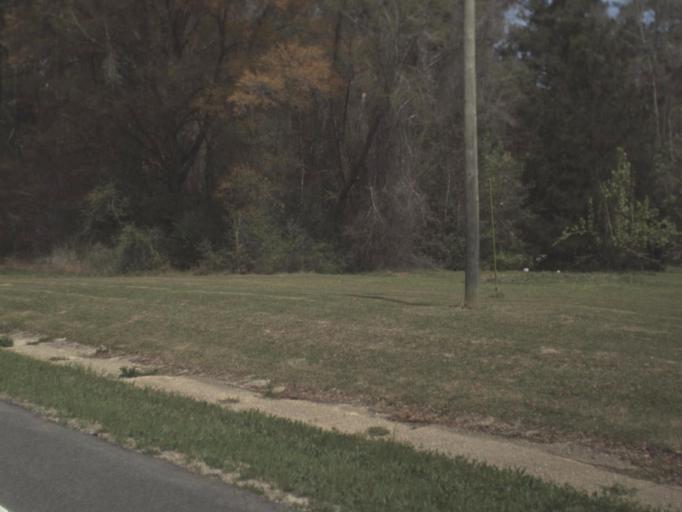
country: US
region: Alabama
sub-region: Geneva County
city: Geneva
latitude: 30.8905
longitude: -85.9522
